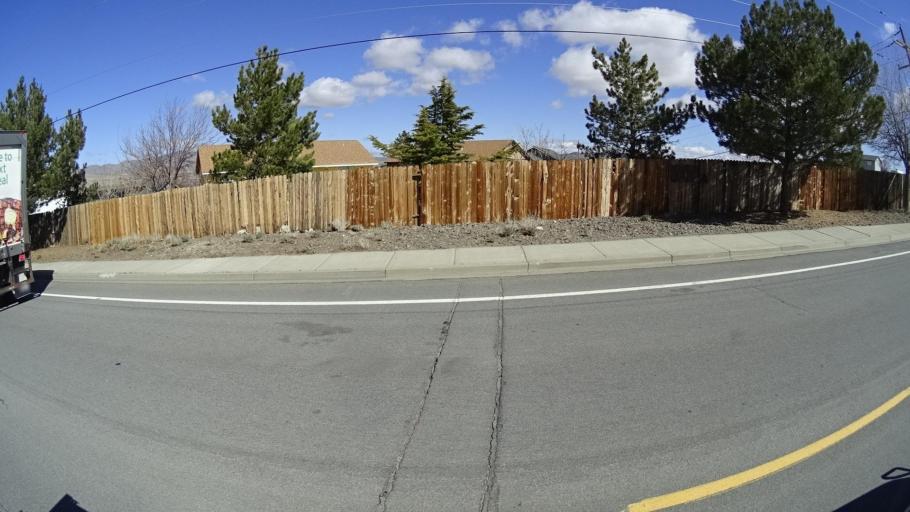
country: US
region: Nevada
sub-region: Washoe County
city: Lemmon Valley
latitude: 39.6265
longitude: -119.9039
